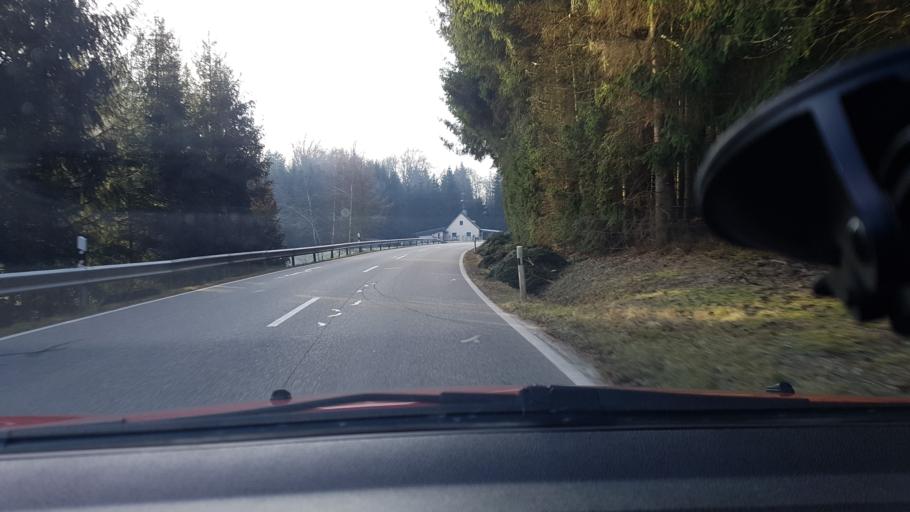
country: DE
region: Bavaria
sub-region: Lower Bavaria
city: Stubenberg
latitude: 48.3010
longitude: 13.0737
